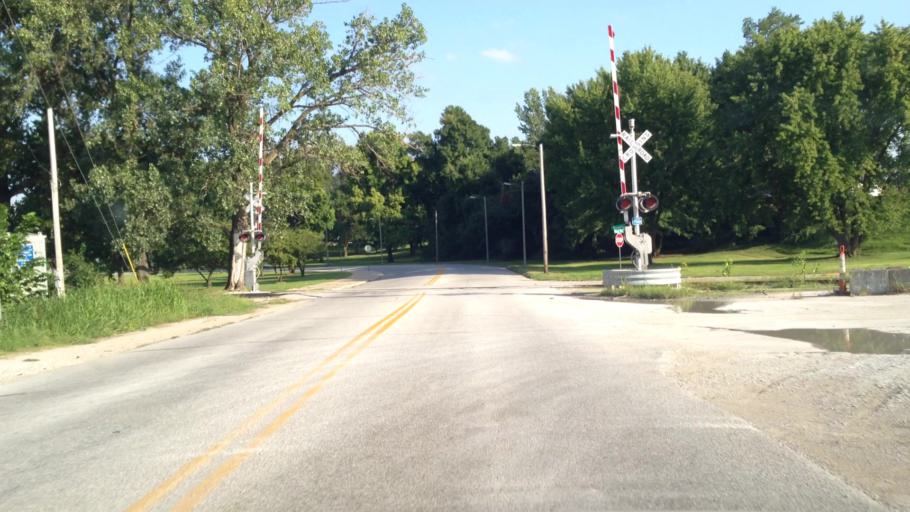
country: US
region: Missouri
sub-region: Jasper County
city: Joplin
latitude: 37.0858
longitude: -94.5055
